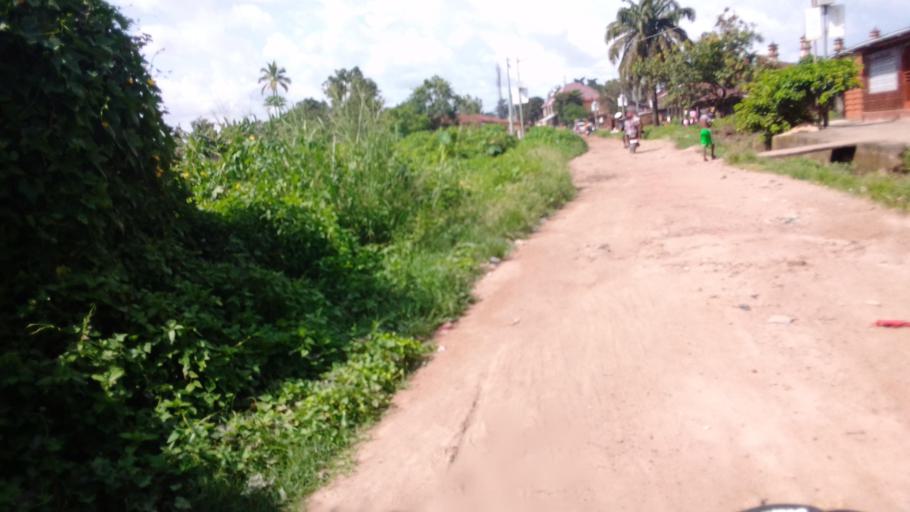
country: SL
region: Northern Province
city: Makeni
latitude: 8.8869
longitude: -12.0408
